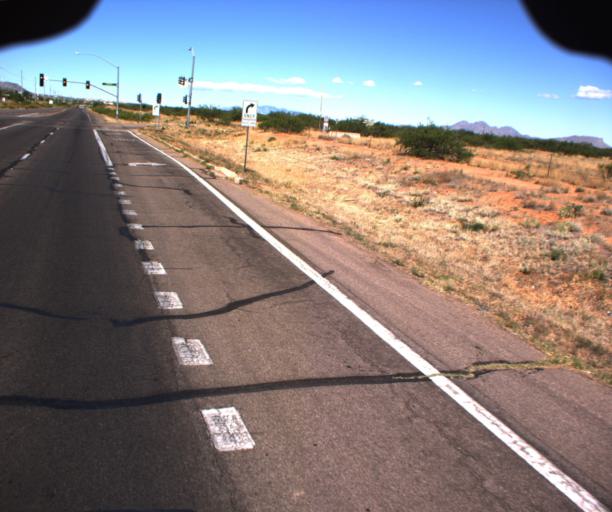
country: US
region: Arizona
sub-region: Cochise County
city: Sierra Vista
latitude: 31.5696
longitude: -110.2904
